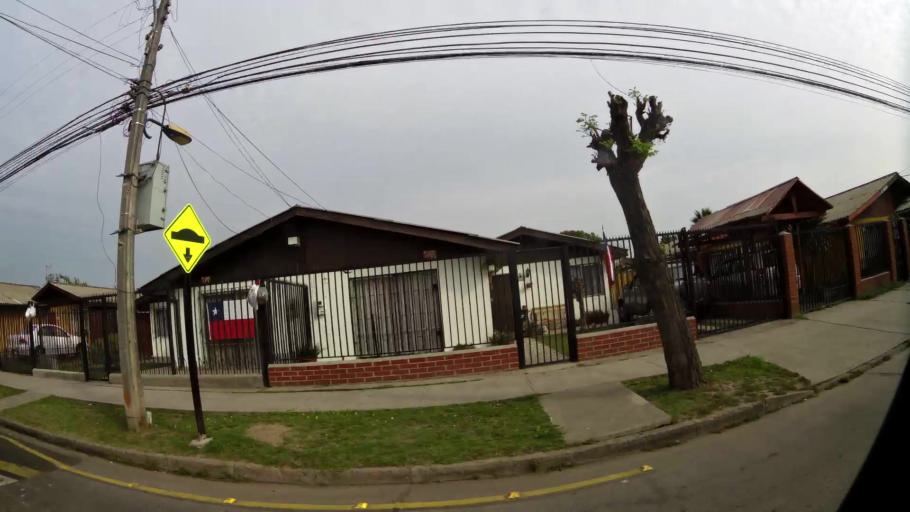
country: CL
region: Santiago Metropolitan
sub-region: Provincia de Santiago
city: Lo Prado
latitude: -33.5195
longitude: -70.7655
